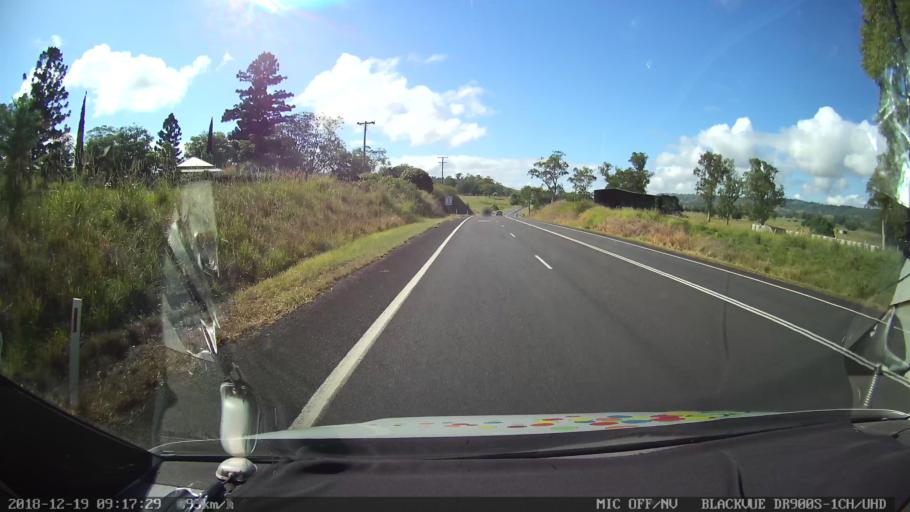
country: AU
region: New South Wales
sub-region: Kyogle
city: Kyogle
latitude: -28.5343
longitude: 152.9743
